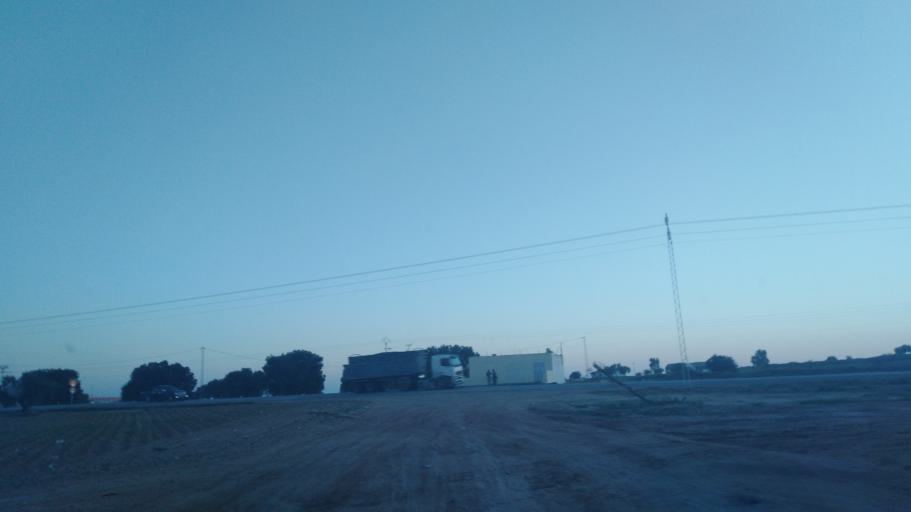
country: TN
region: Safaqis
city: Sfax
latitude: 34.7255
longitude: 10.4472
